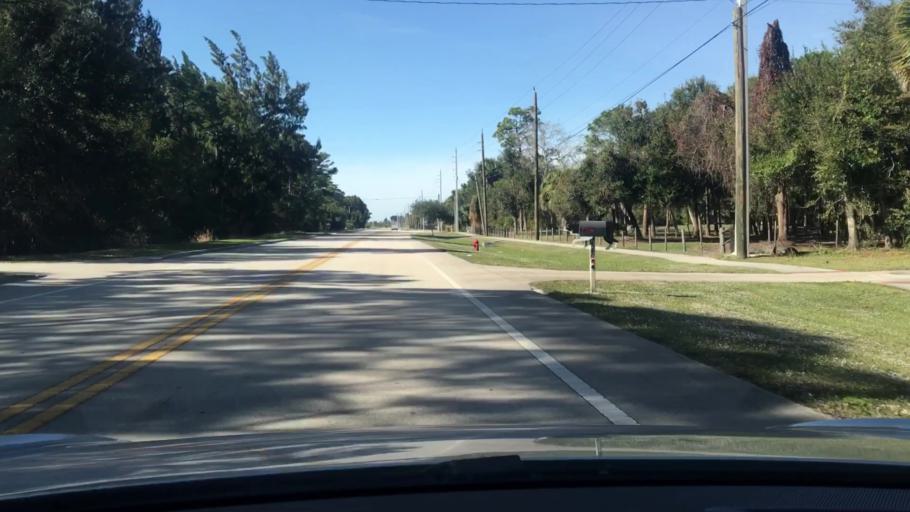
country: US
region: Florida
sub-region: Indian River County
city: Winter Beach
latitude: 27.6972
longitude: -80.4519
